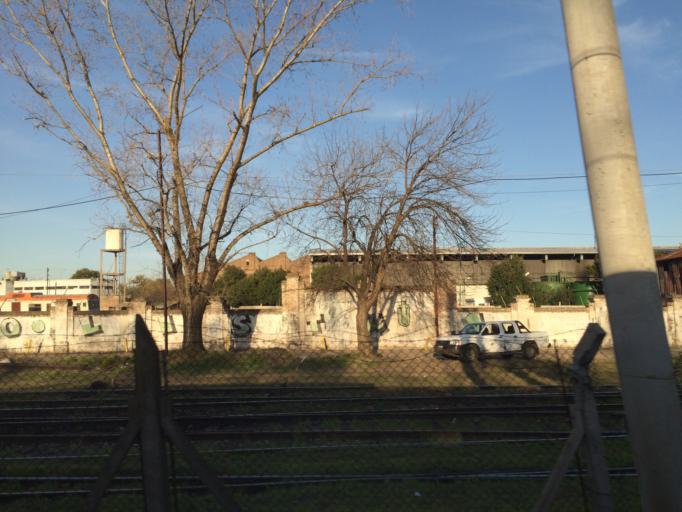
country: AR
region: Buenos Aires
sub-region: Partido de Lanus
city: Lanus
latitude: -34.7256
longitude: -58.3933
